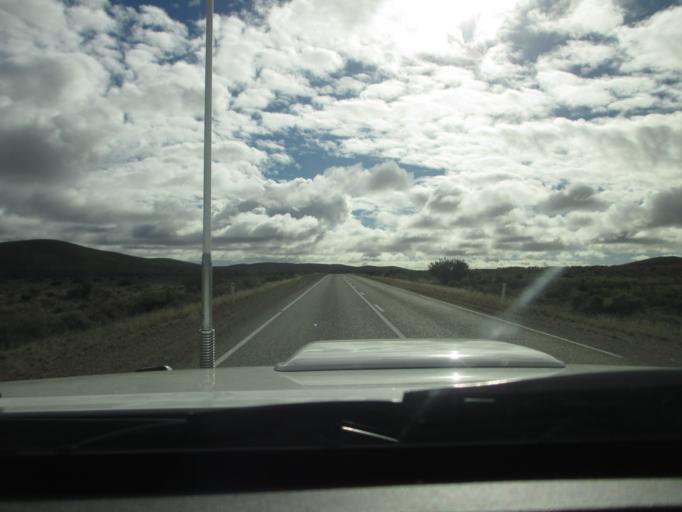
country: AU
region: South Australia
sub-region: Flinders Ranges
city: Quorn
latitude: -32.2217
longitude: 138.5181
